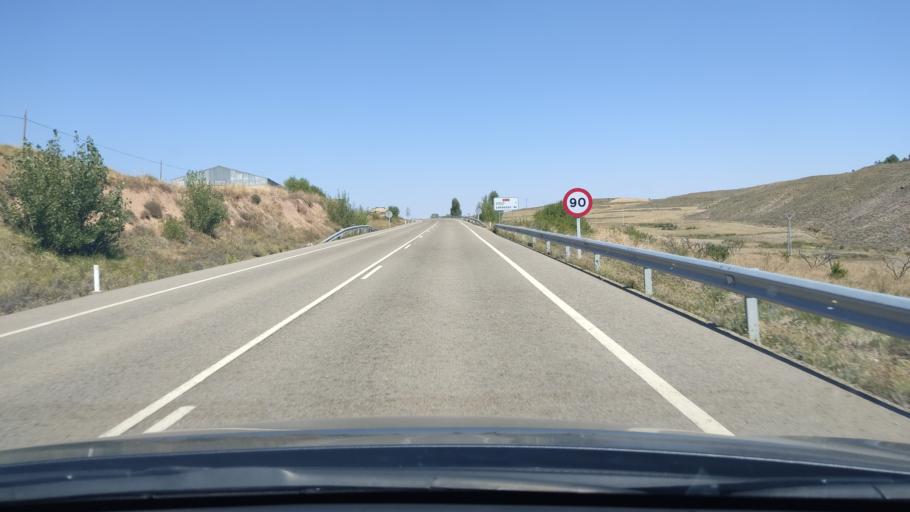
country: ES
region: Aragon
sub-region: Provincia de Teruel
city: Cortes de Aragon
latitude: 40.9287
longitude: -0.8425
